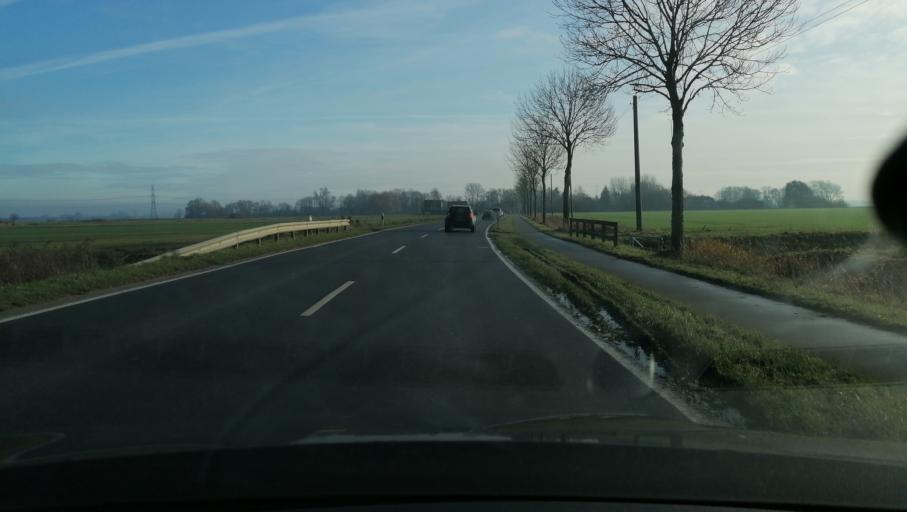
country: DE
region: Schleswig-Holstein
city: Epenwohrden
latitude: 54.1111
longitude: 9.0231
